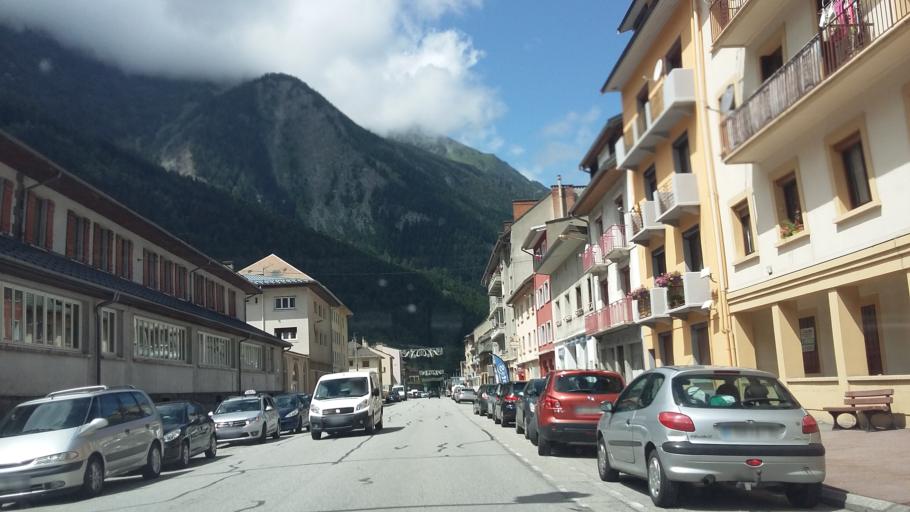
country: FR
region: Rhone-Alpes
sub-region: Departement de la Savoie
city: Modane
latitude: 45.1920
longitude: 6.6516
